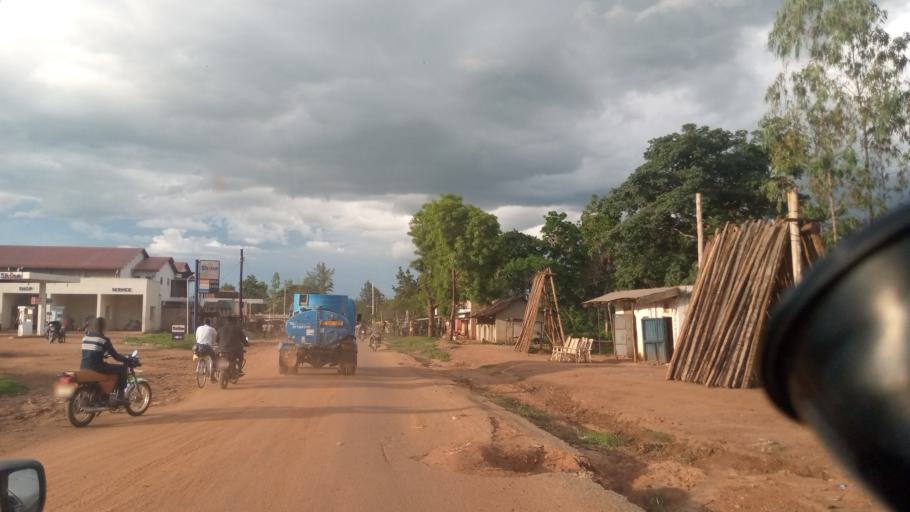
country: UG
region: Northern Region
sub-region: Lira District
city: Lira
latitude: 2.2633
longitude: 32.9101
